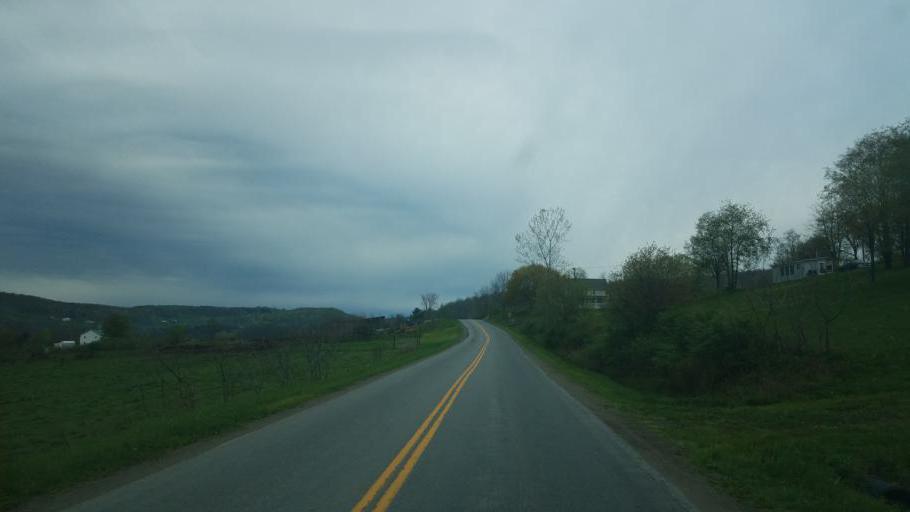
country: US
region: Pennsylvania
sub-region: Tioga County
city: Elkland
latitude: 42.0824
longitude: -77.4440
